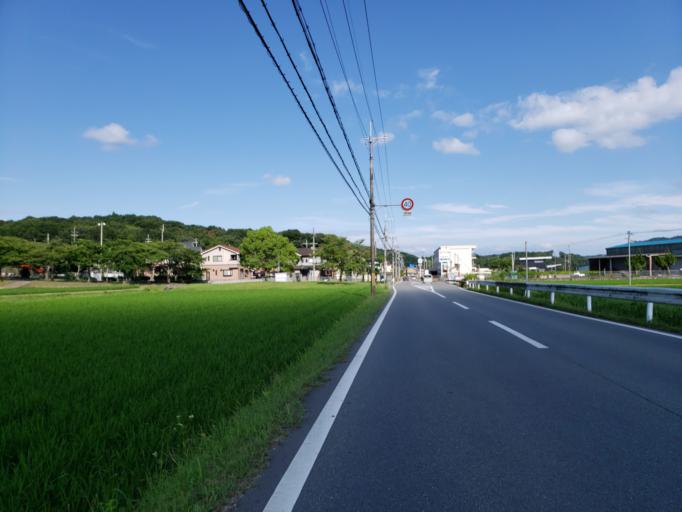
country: JP
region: Hyogo
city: Himeji
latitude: 34.9064
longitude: 134.7898
